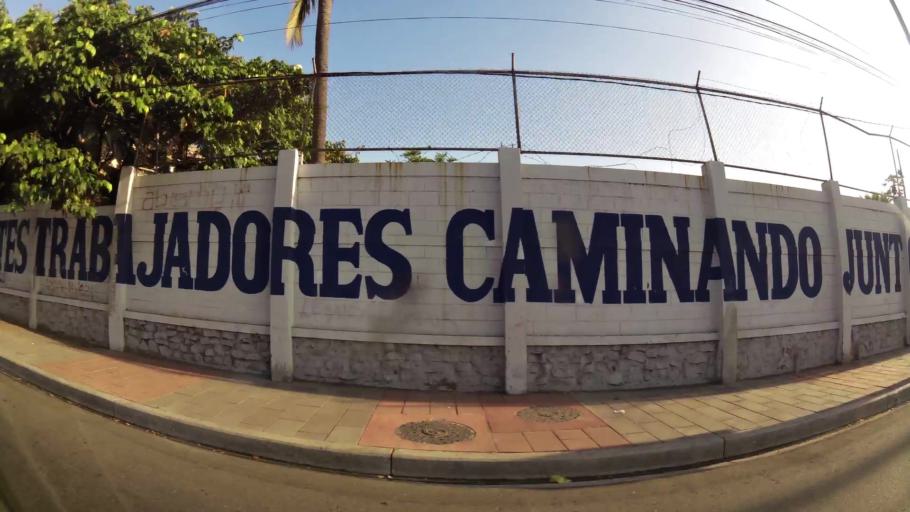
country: EC
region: Guayas
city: Guayaquil
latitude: -2.1794
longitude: -79.8989
